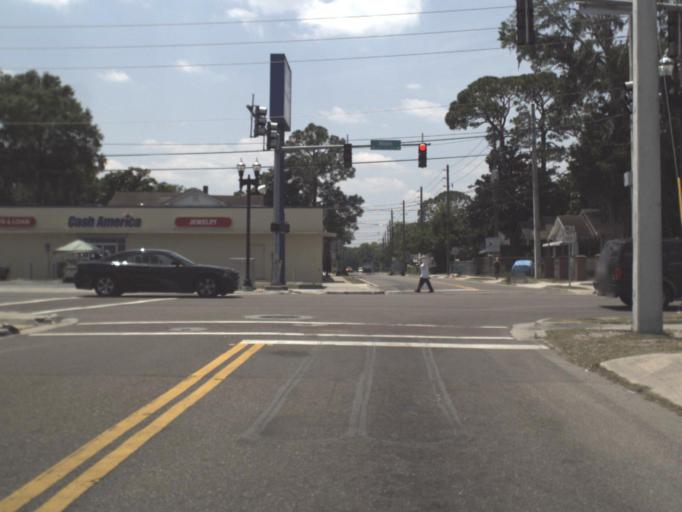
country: US
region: Florida
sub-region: Duval County
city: Jacksonville
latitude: 30.3608
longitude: -81.6532
